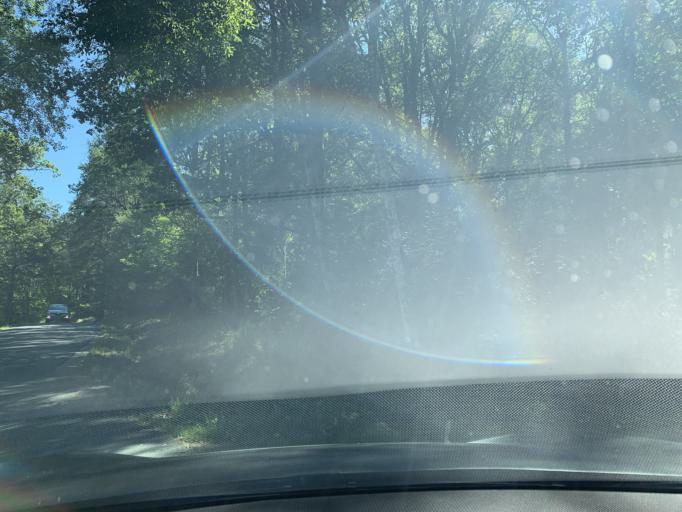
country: SE
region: Stockholm
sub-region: Botkyrka Kommun
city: Eriksberg
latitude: 59.2513
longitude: 17.7700
